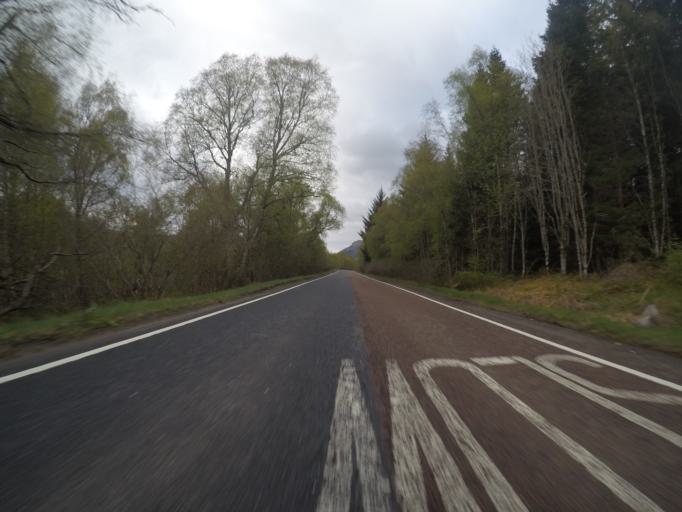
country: GB
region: Scotland
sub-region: Highland
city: Kingussie
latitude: 56.9694
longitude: -4.4378
